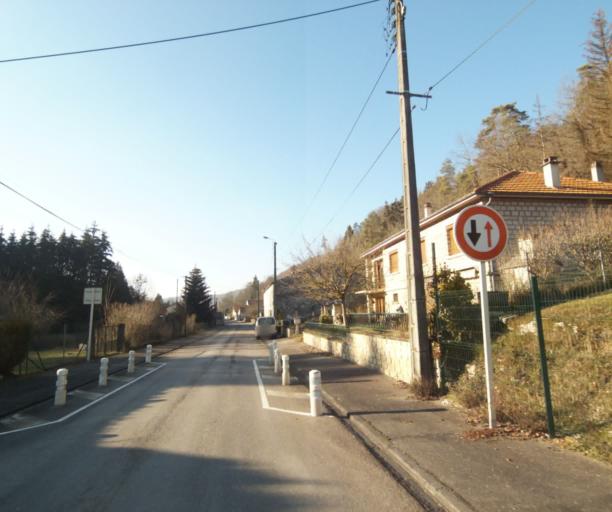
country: FR
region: Champagne-Ardenne
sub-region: Departement de la Haute-Marne
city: Chevillon
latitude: 48.5269
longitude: 5.1487
